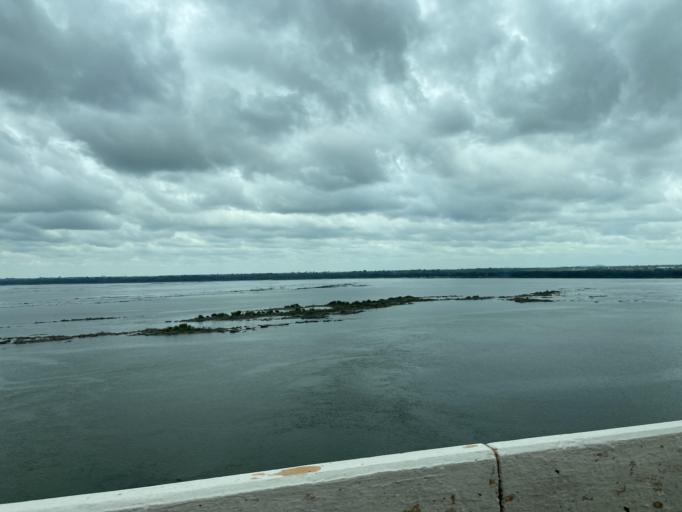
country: BR
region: Para
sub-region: Maraba
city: Maraba
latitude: -5.3191
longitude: -49.0819
